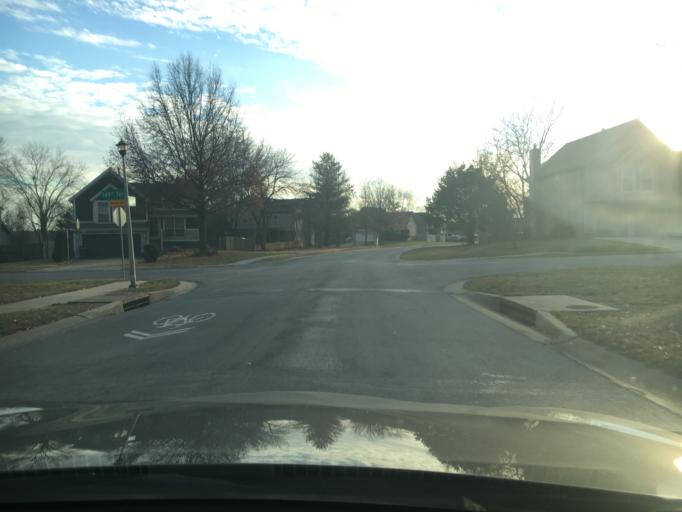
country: US
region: Kansas
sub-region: Johnson County
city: Lenexa
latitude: 38.8579
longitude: -94.6803
